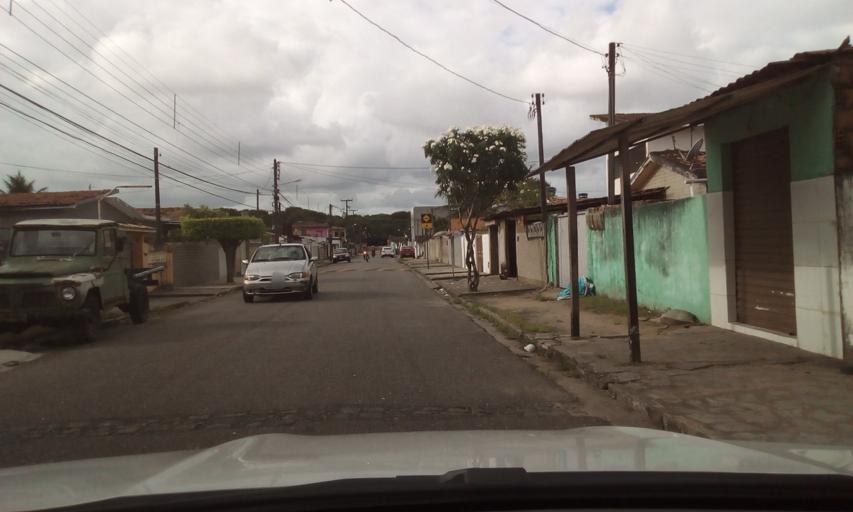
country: BR
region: Paraiba
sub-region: Joao Pessoa
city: Joao Pessoa
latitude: -7.1487
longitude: -34.8769
